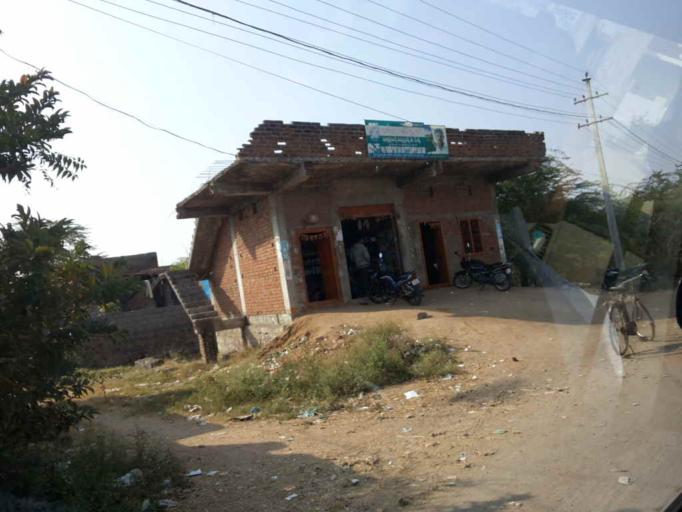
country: IN
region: Telangana
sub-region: Karimnagar
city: Vemalwada
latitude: 18.3927
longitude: 78.9898
